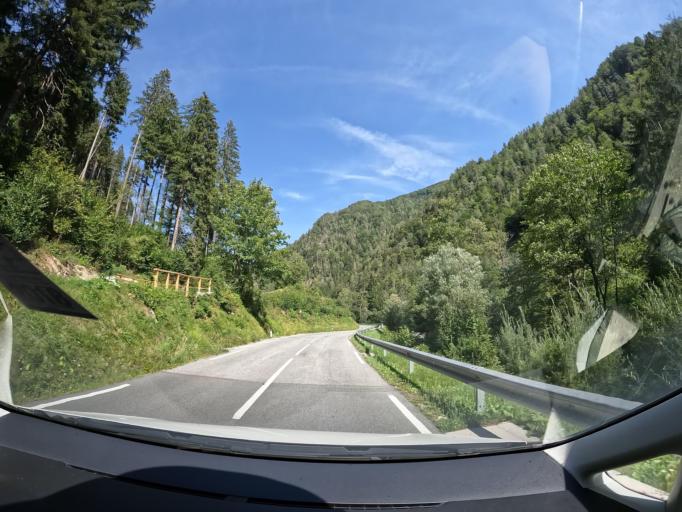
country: SI
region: Jesenice
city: Koroska Bela
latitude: 46.4472
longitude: 14.1524
